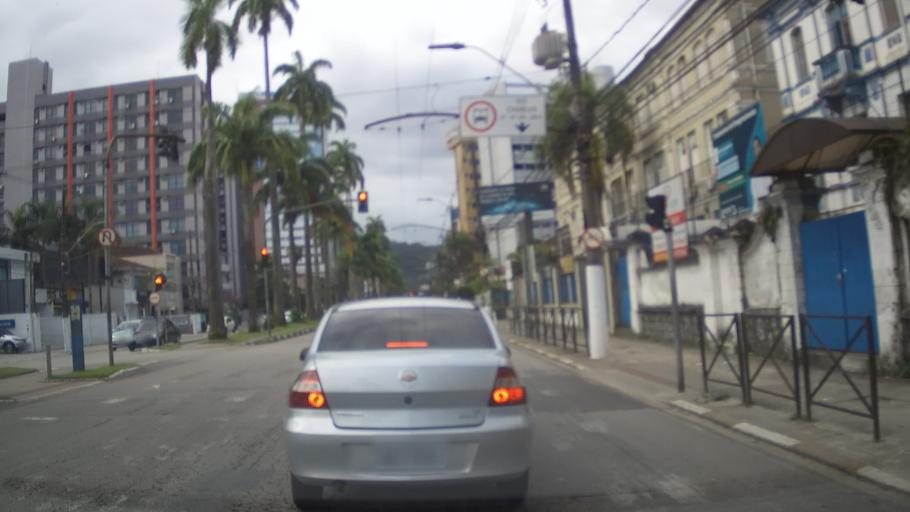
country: BR
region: Sao Paulo
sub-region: Santos
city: Santos
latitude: -23.9565
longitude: -46.3314
